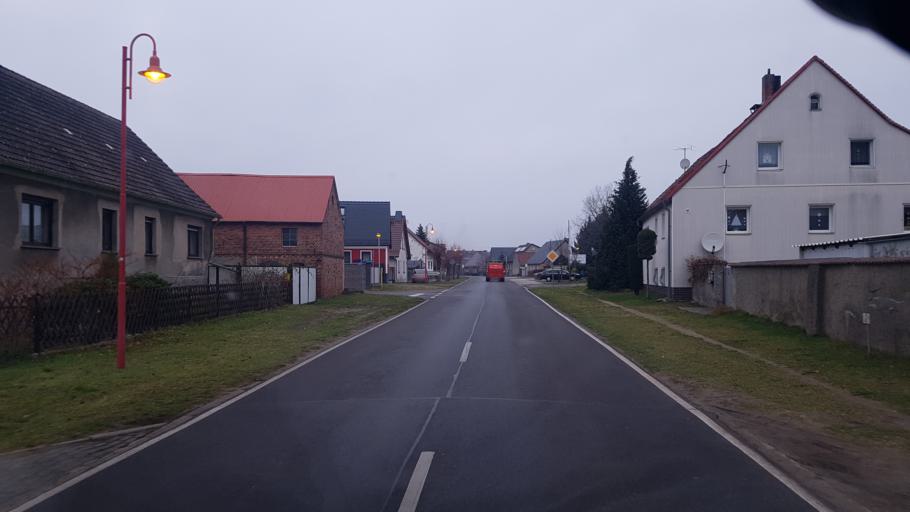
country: DE
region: Brandenburg
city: Schenkendobern
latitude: 51.9569
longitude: 14.6360
